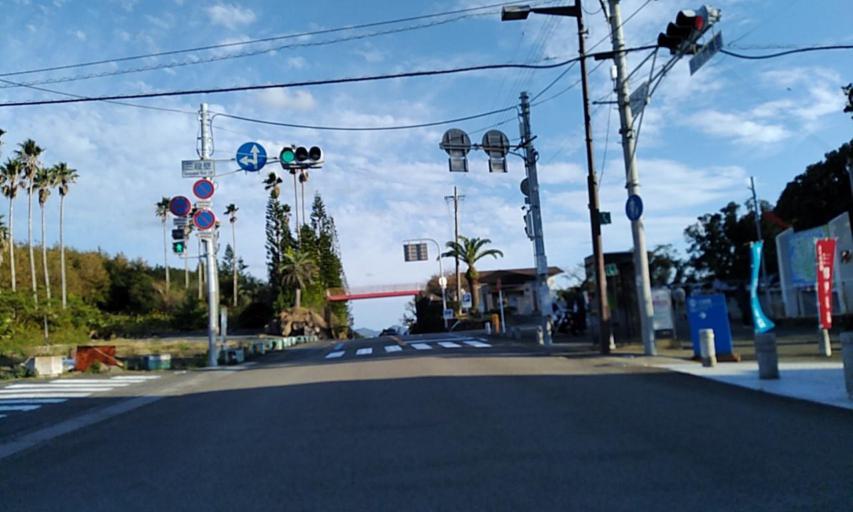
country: JP
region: Wakayama
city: Tanabe
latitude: 33.6664
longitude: 135.3369
